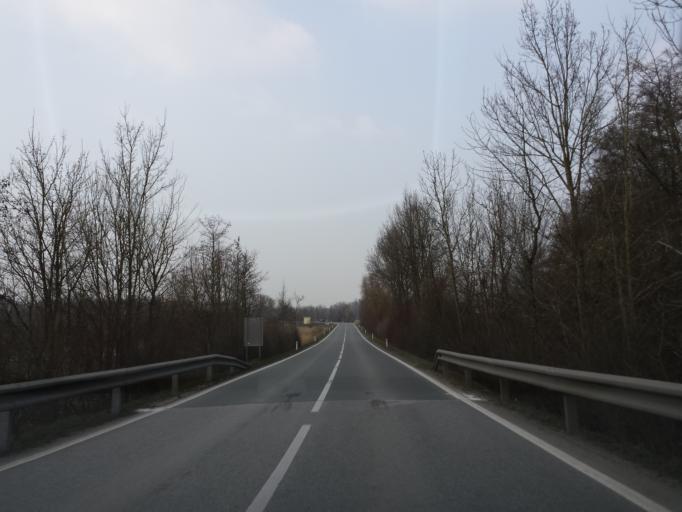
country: AT
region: Styria
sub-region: Politischer Bezirk Hartberg-Fuerstenfeld
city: Fuerstenfeld
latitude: 47.0427
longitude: 16.0990
